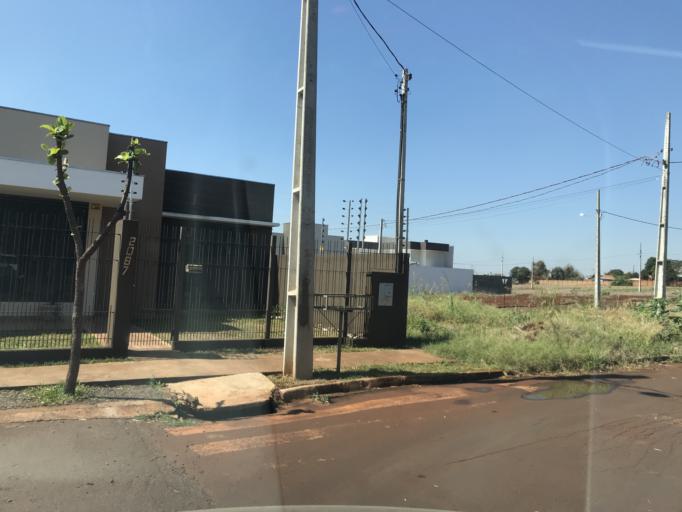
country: BR
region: Parana
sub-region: Palotina
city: Palotina
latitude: -24.2932
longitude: -53.8354
